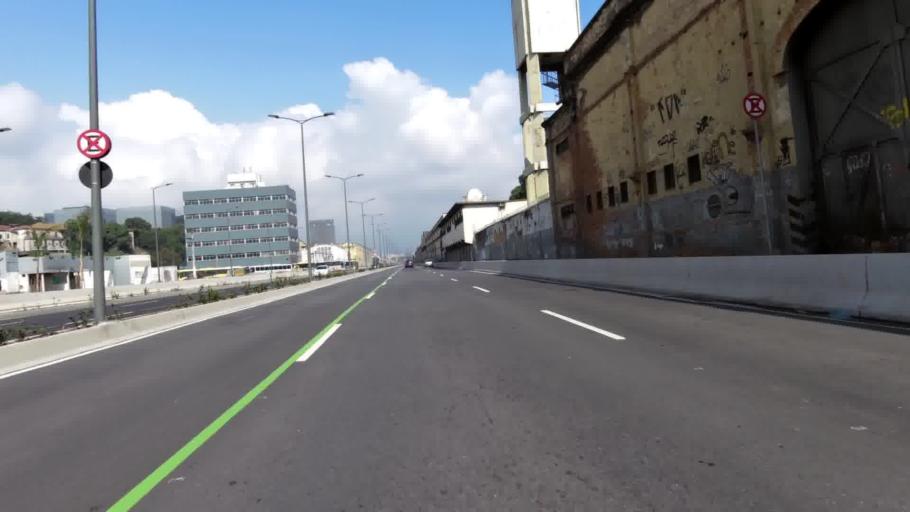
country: BR
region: Rio de Janeiro
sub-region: Rio De Janeiro
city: Rio de Janeiro
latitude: -22.8939
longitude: -43.1987
